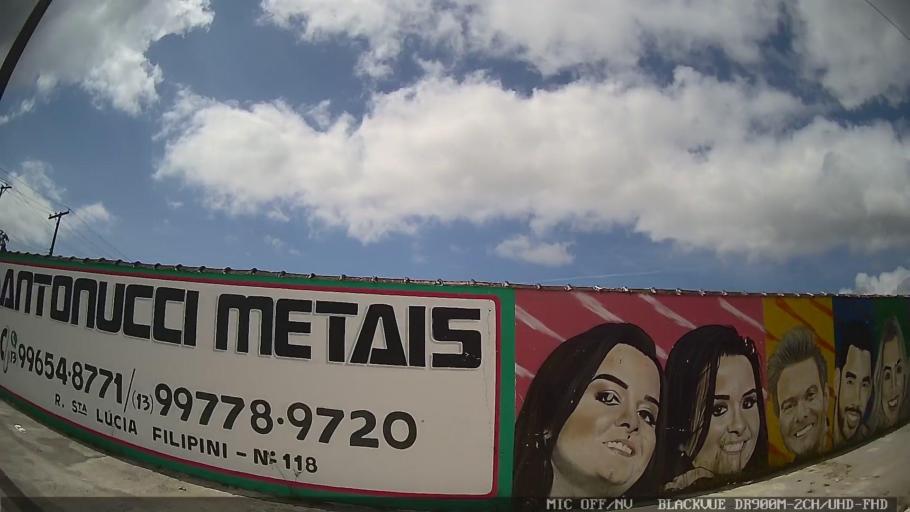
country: BR
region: Sao Paulo
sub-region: Peruibe
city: Peruibe
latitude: -24.2940
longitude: -47.0205
